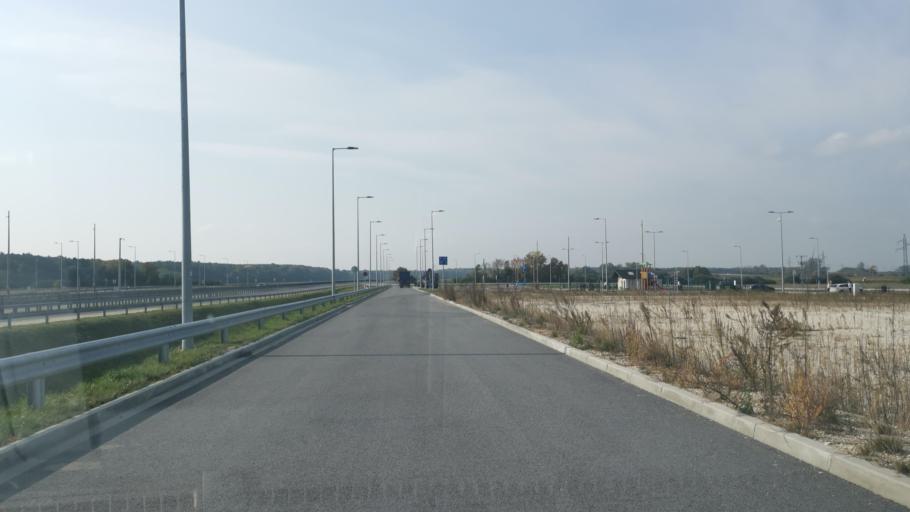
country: HU
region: Gyor-Moson-Sopron
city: Mihalyi
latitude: 47.5640
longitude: 17.0871
